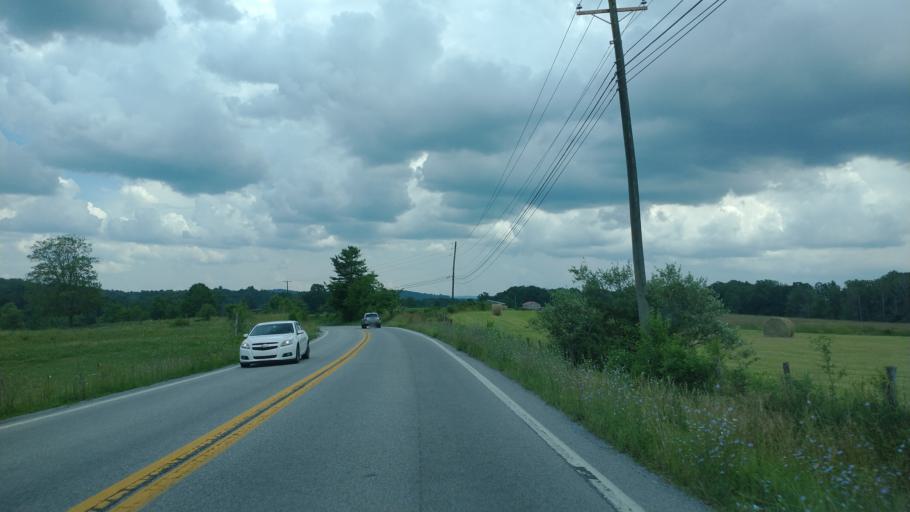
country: US
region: West Virginia
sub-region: Mercer County
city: Athens
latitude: 37.4508
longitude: -81.0069
